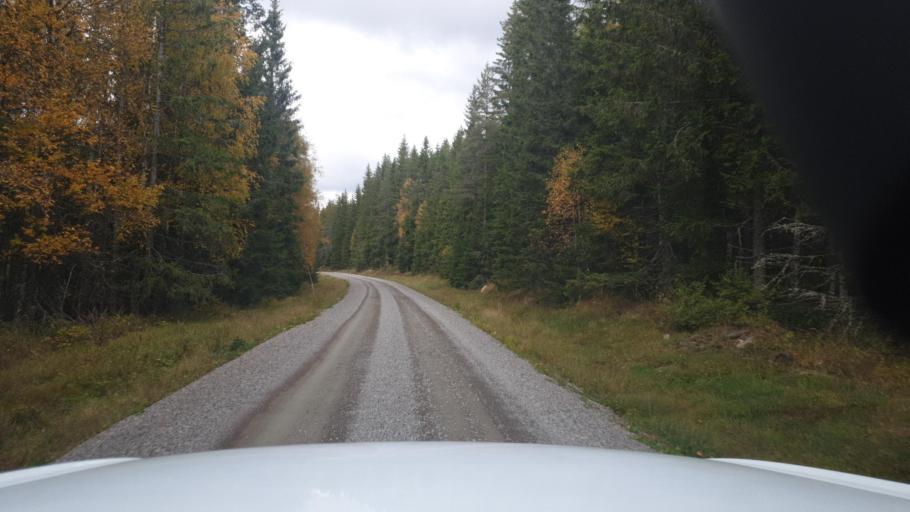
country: SE
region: Vaermland
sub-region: Eda Kommun
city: Charlottenberg
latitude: 60.0805
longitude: 12.6197
